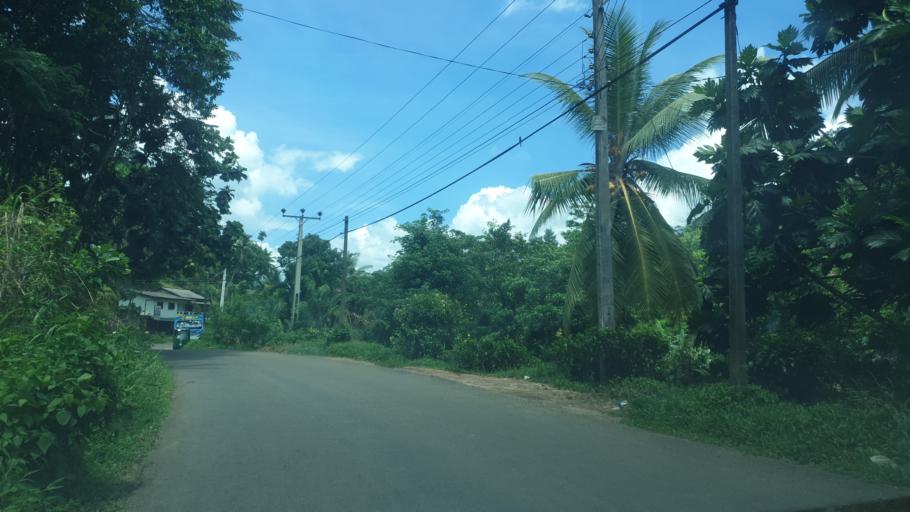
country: LK
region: Sabaragamuwa
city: Ratnapura
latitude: 6.4860
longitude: 80.4043
